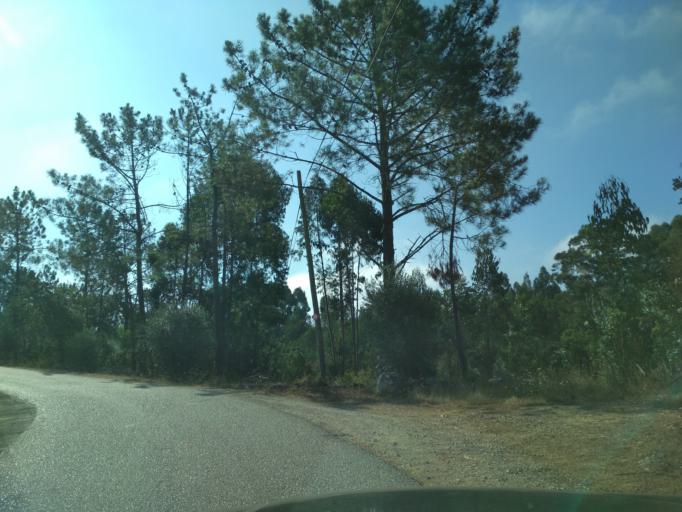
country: PT
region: Coimbra
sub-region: Soure
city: Soure
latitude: 39.9929
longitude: -8.5737
